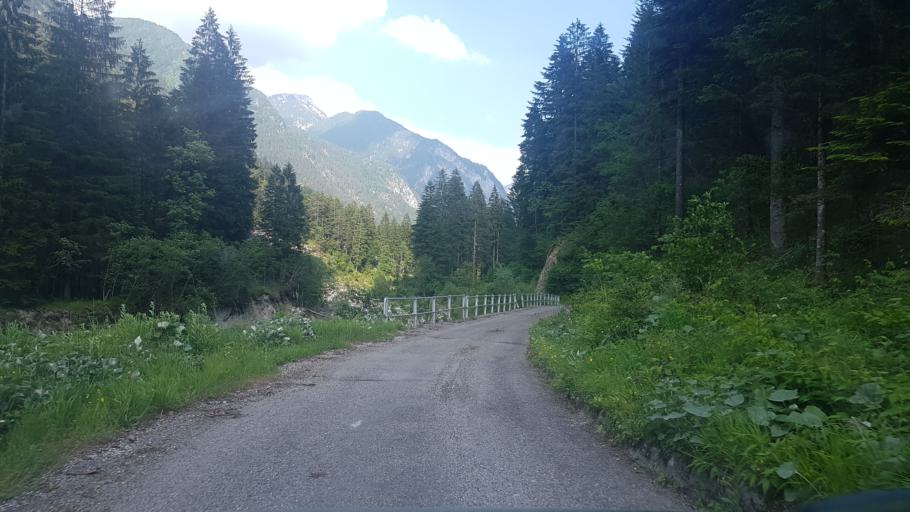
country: IT
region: Friuli Venezia Giulia
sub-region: Provincia di Udine
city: Pontebba
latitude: 46.5249
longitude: 13.2289
